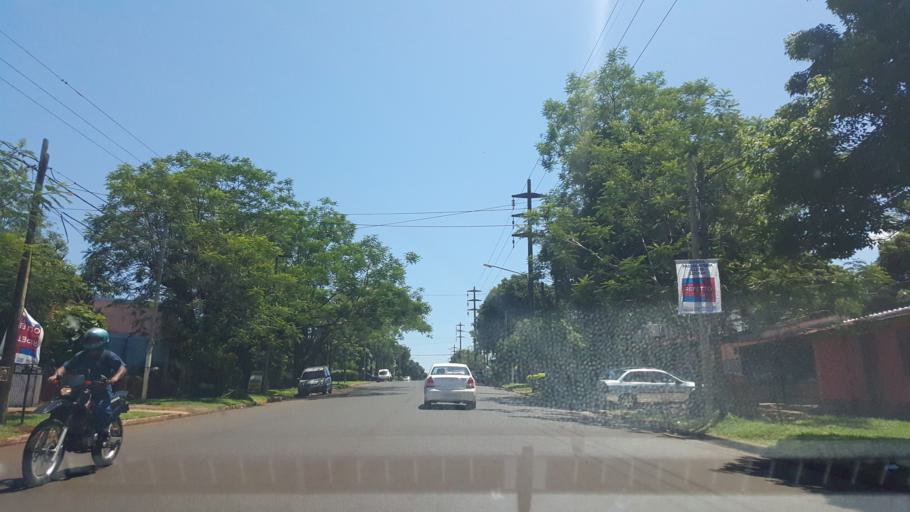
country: AR
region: Misiones
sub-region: Departamento de Capital
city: Posadas
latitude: -27.3751
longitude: -55.9219
